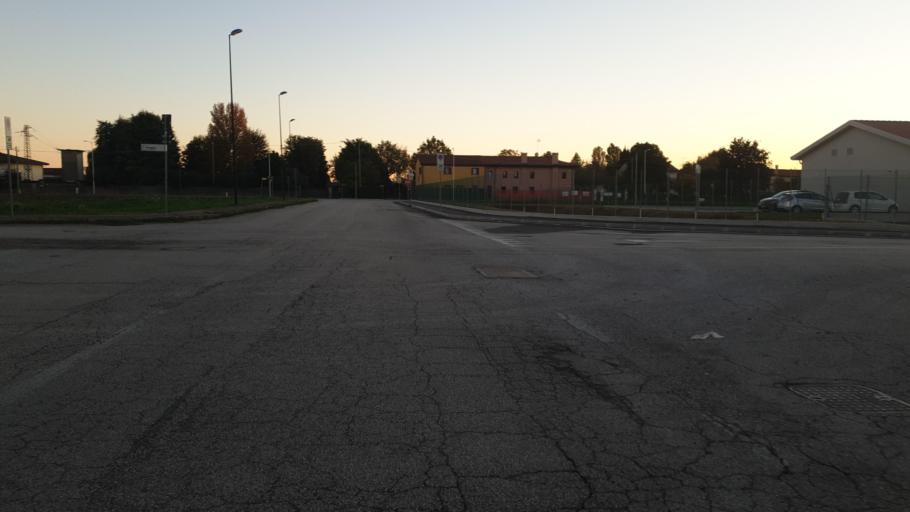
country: IT
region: Veneto
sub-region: Provincia di Venezia
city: Cazzago-Ex Polo
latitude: 45.4410
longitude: 12.0645
